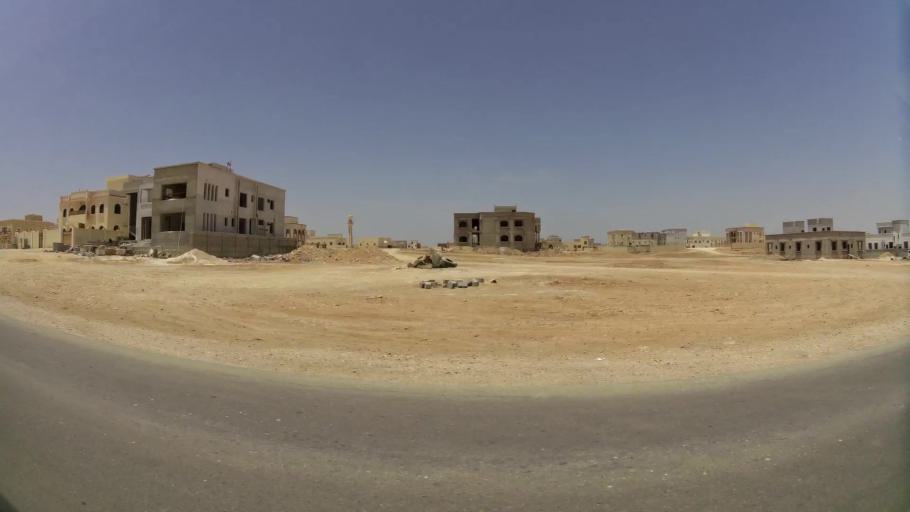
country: OM
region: Zufar
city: Salalah
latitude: 17.0918
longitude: 54.2013
